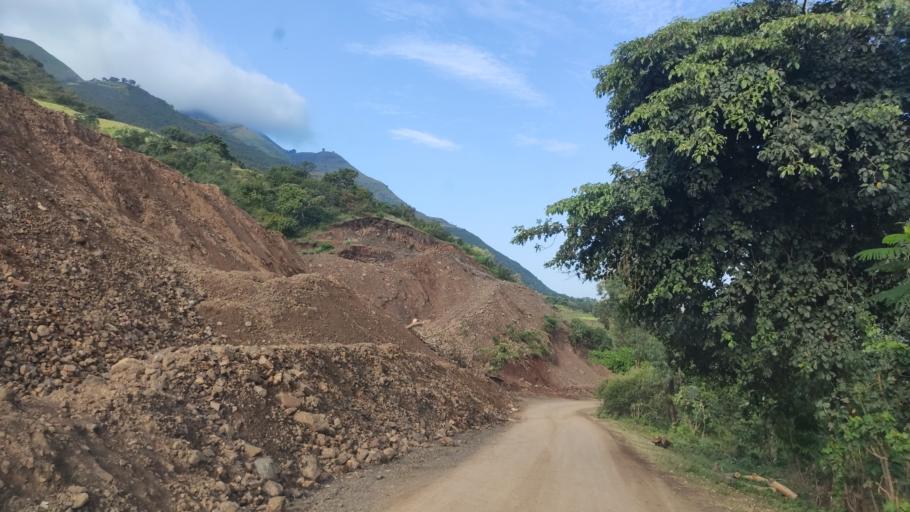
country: ET
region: Southern Nations, Nationalities, and People's Region
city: Arba Minch'
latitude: 6.4239
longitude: 37.3654
